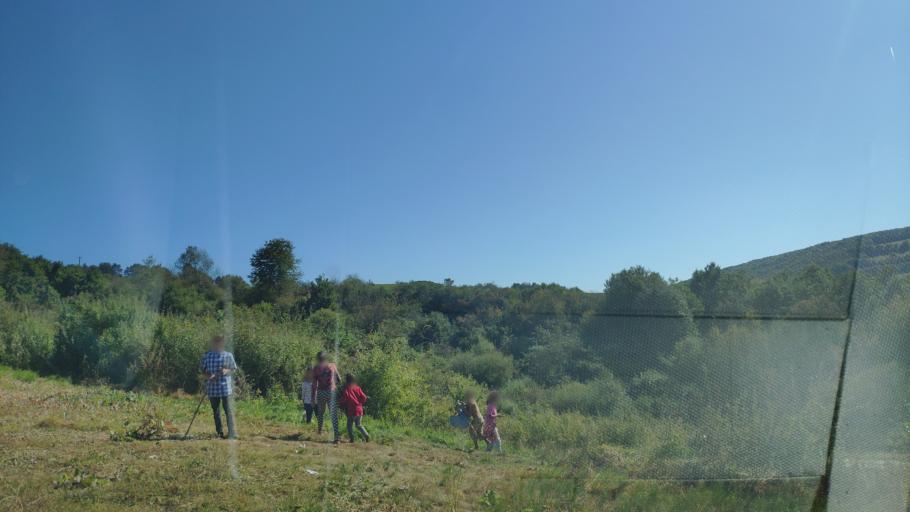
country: SK
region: Presovsky
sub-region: Okres Presov
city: Presov
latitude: 48.9643
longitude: 21.1422
